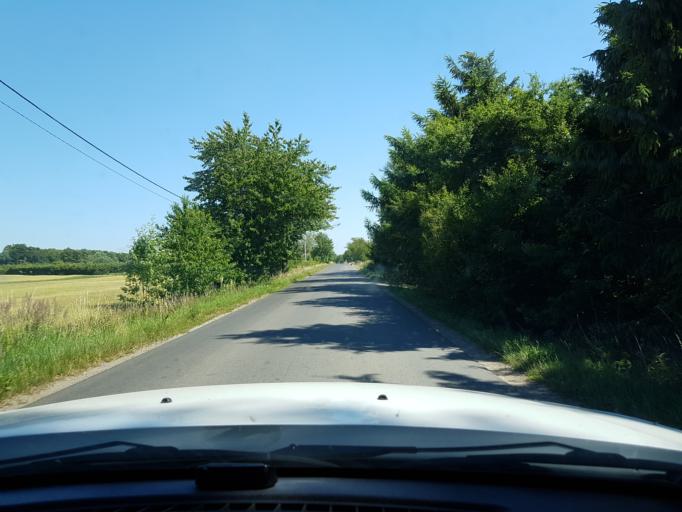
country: PL
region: West Pomeranian Voivodeship
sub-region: Powiat koszalinski
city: Mielno
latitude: 54.1905
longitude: 16.0588
